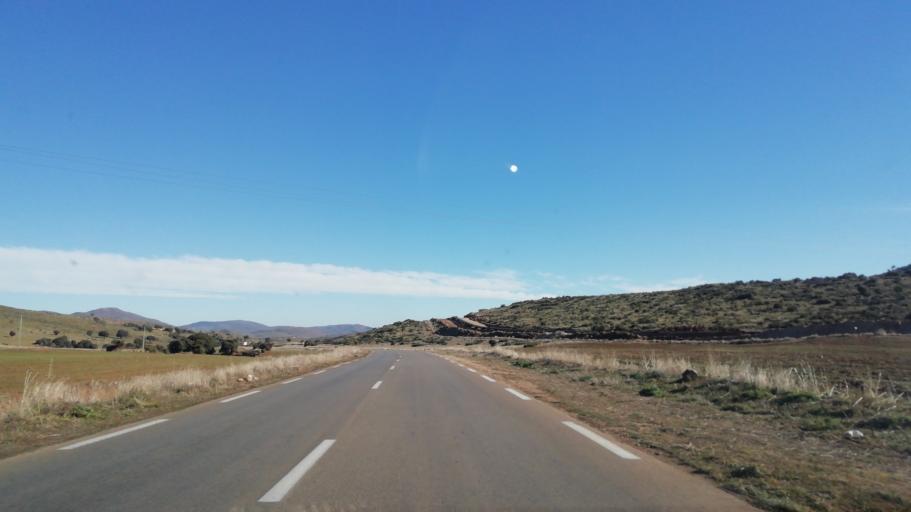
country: DZ
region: Tlemcen
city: Ouled Mimoun
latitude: 34.7498
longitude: -1.1584
